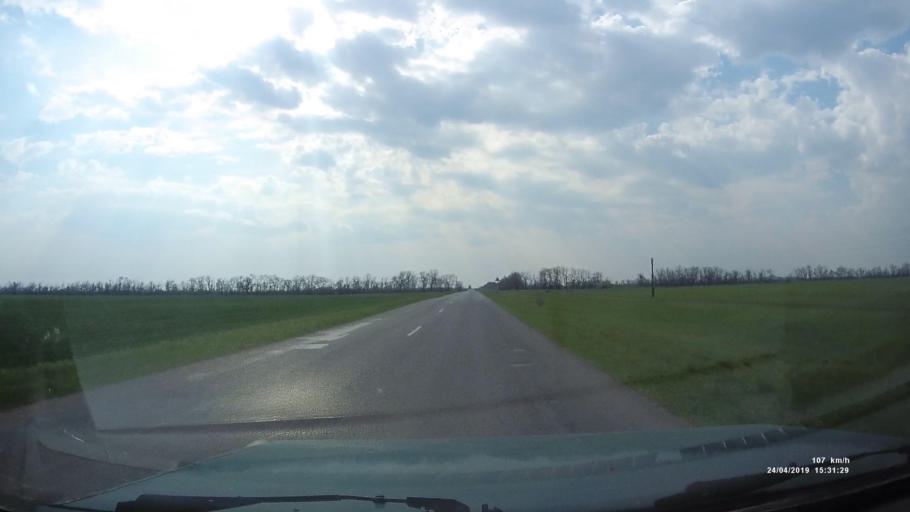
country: RU
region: Rostov
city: Remontnoye
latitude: 46.5996
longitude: 42.9826
